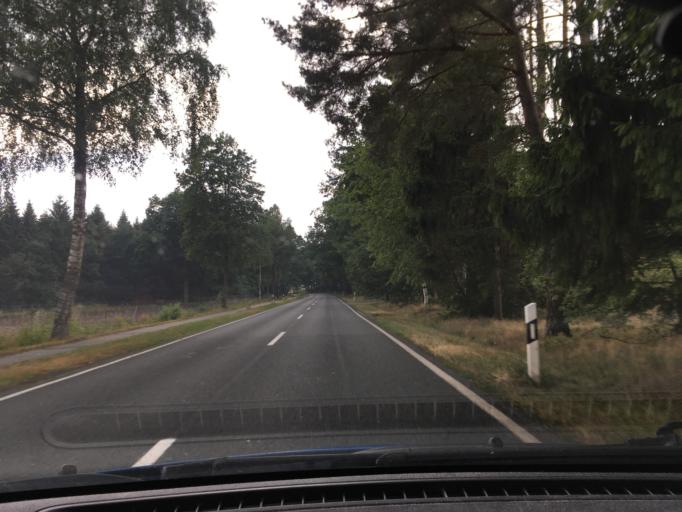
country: DE
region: Lower Saxony
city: Hollenstedt
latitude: 53.3583
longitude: 9.7309
